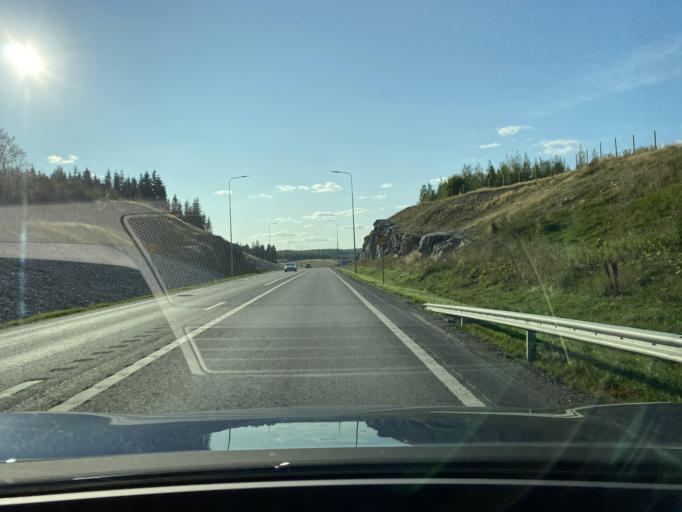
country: FI
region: Paijanne Tavastia
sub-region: Lahti
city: Hollola
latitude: 60.9598
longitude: 25.5426
